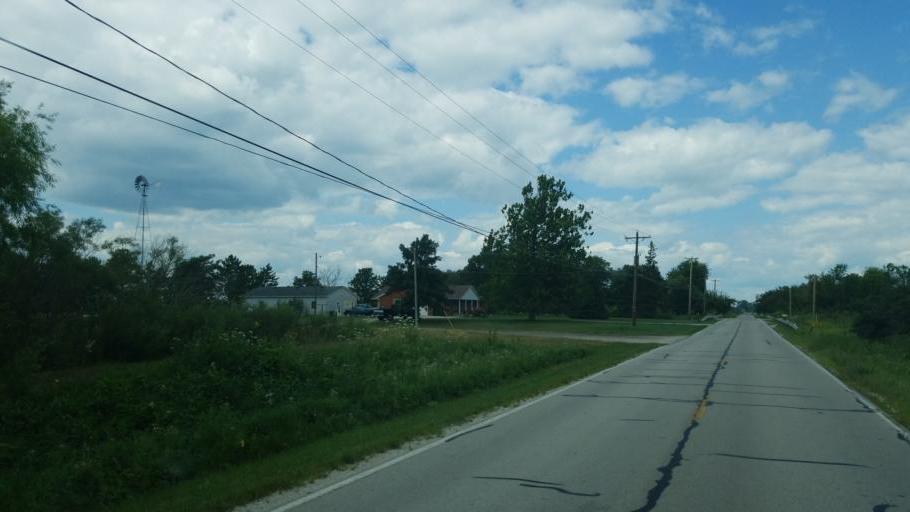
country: US
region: Ohio
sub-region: Lucas County
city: Curtice
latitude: 41.6228
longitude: -83.2794
